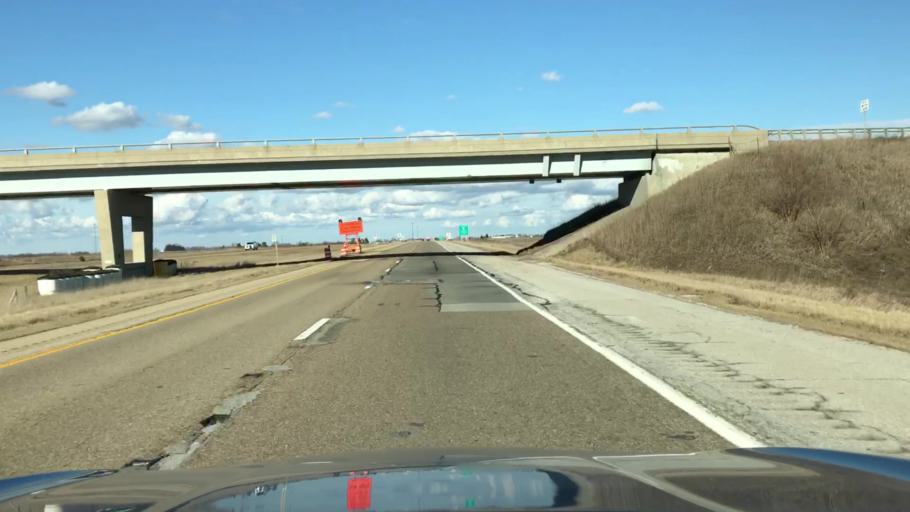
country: US
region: Illinois
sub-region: McLean County
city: Chenoa
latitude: 40.7265
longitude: -88.7370
